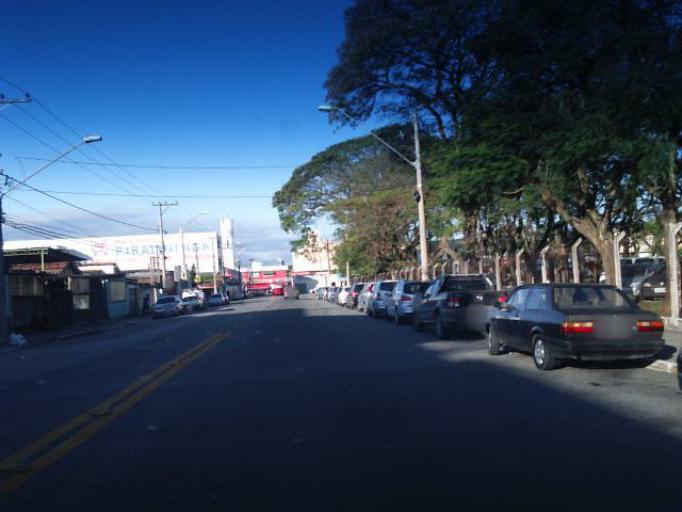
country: BR
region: Sao Paulo
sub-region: Sao Jose Dos Campos
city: Sao Jose dos Campos
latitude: -23.1923
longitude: -45.8781
